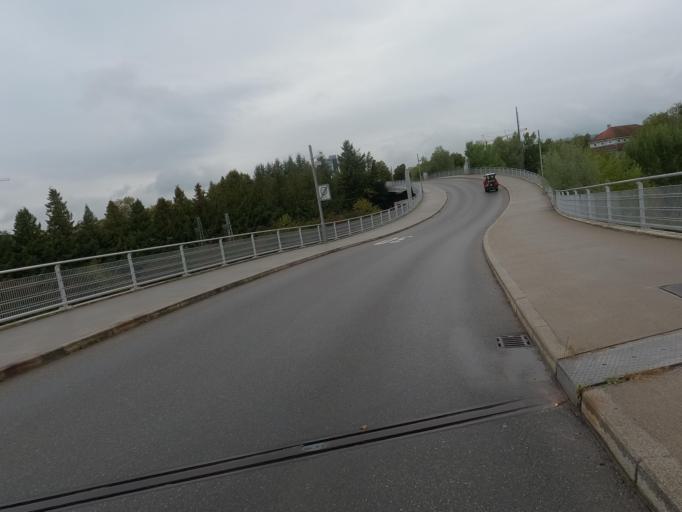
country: DE
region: Baden-Wuerttemberg
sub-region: Freiburg Region
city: Radolfzell am Bodensee
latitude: 47.7386
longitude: 8.9781
